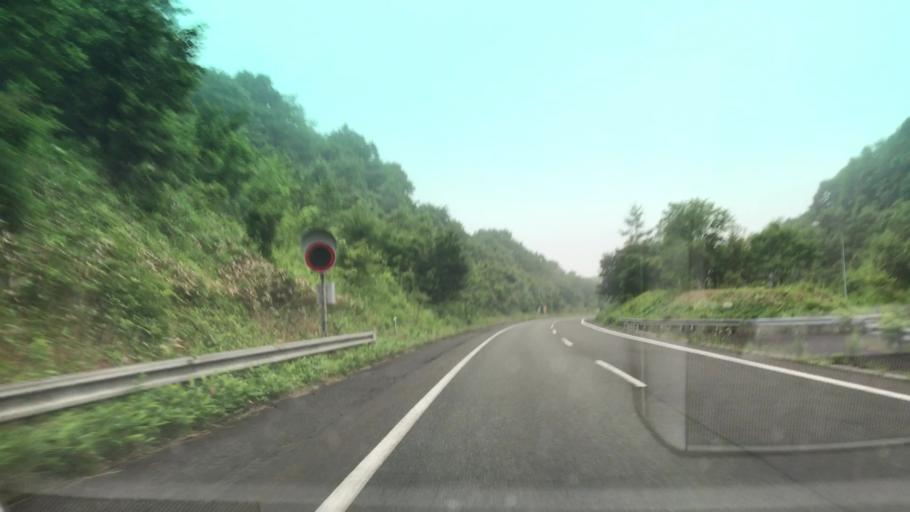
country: JP
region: Hokkaido
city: Shiraoi
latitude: 42.4719
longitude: 141.2130
